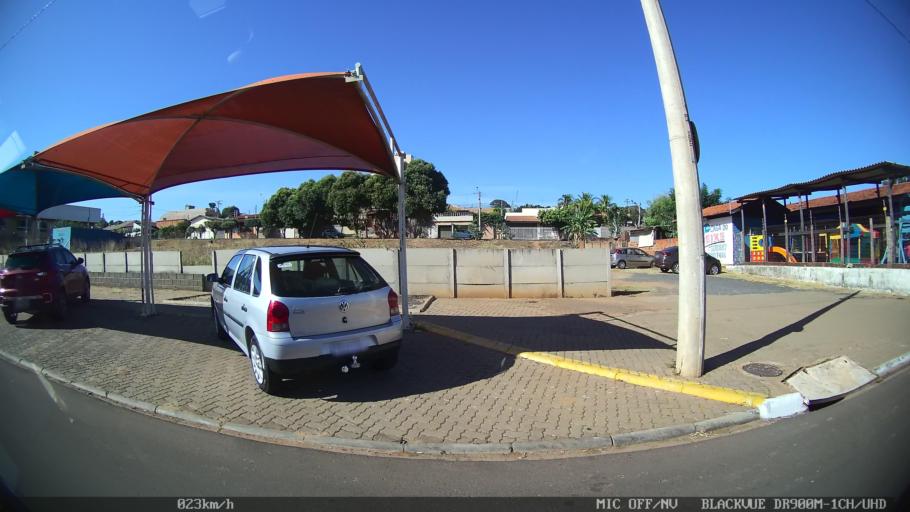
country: BR
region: Sao Paulo
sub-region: Olimpia
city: Olimpia
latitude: -20.7338
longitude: -48.9122
